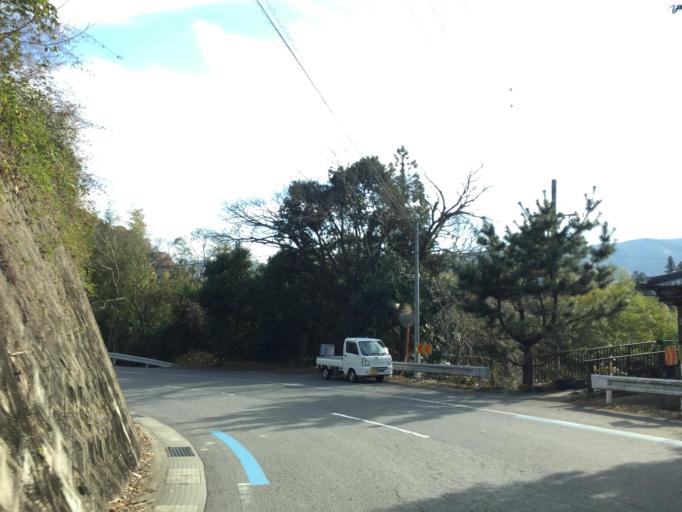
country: JP
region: Wakayama
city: Iwade
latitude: 34.1496
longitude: 135.3723
